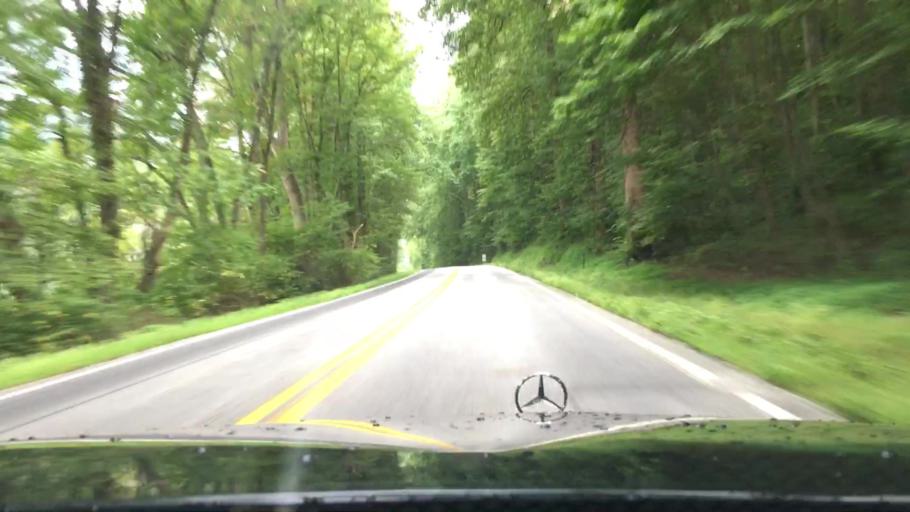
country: US
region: Virginia
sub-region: Nelson County
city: Nellysford
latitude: 37.8408
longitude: -78.9278
